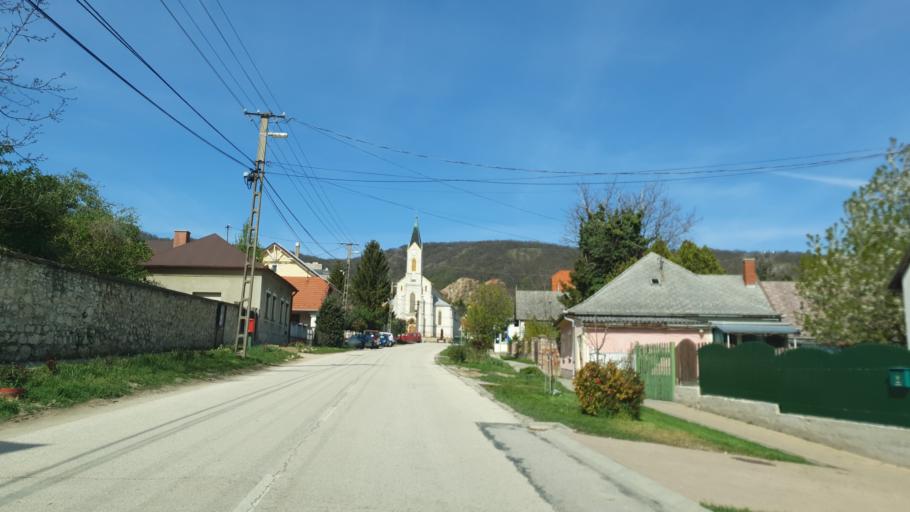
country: HU
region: Fejer
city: Bodajk
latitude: 47.3523
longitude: 18.2717
